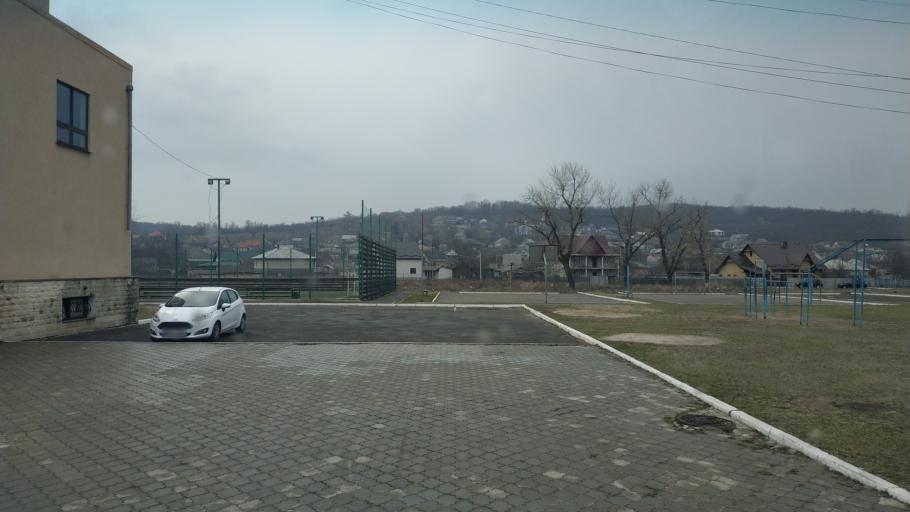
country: MD
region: Chisinau
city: Singera
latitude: 46.9141
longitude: 28.9737
